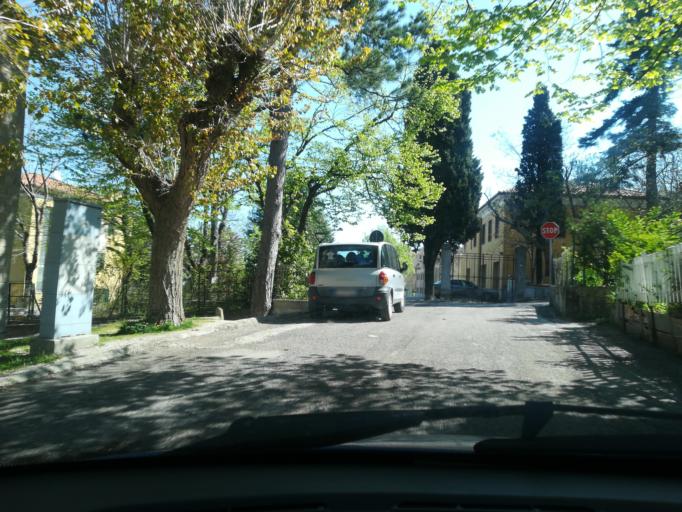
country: IT
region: The Marches
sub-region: Provincia di Macerata
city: Cingoli
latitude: 43.3766
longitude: 13.2100
